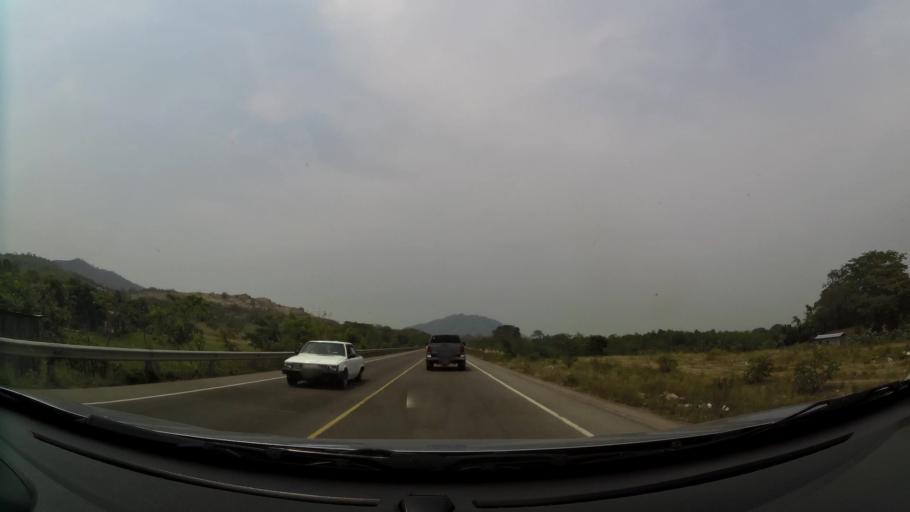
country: HN
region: Cortes
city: Potrerillos
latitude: 15.2388
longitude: -87.9575
